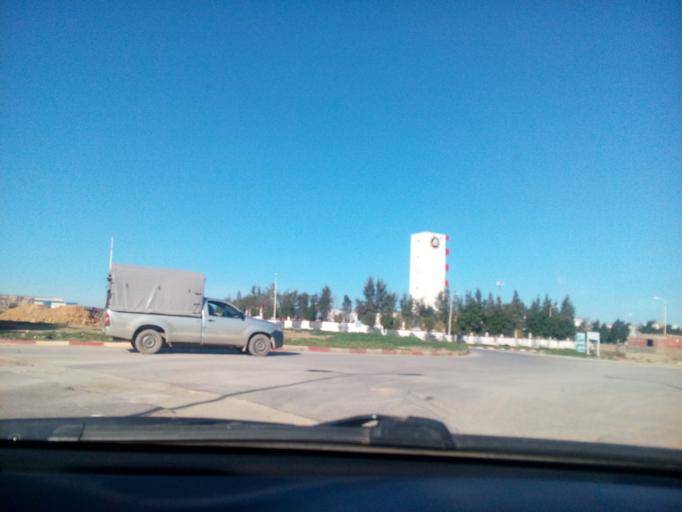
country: DZ
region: Relizane
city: Relizane
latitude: 35.7190
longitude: 0.5290
